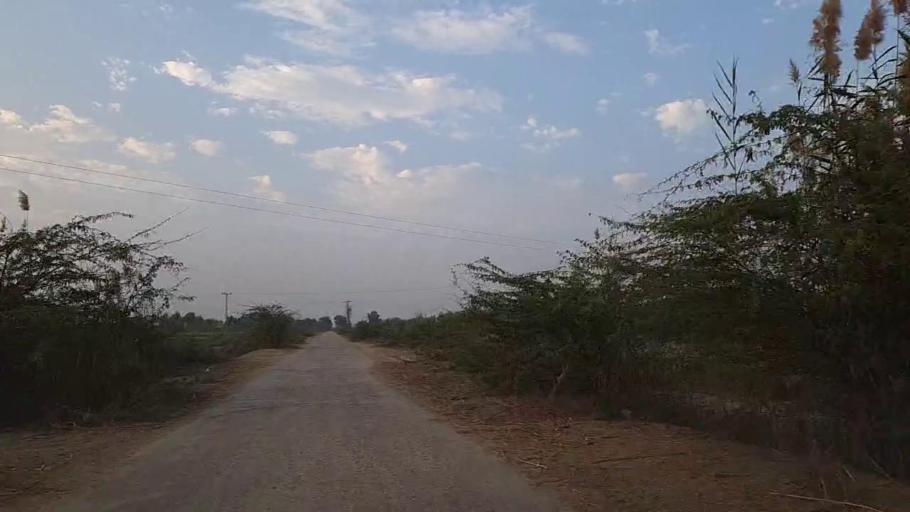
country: PK
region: Sindh
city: Mirwah Gorchani
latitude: 25.3382
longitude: 69.2088
